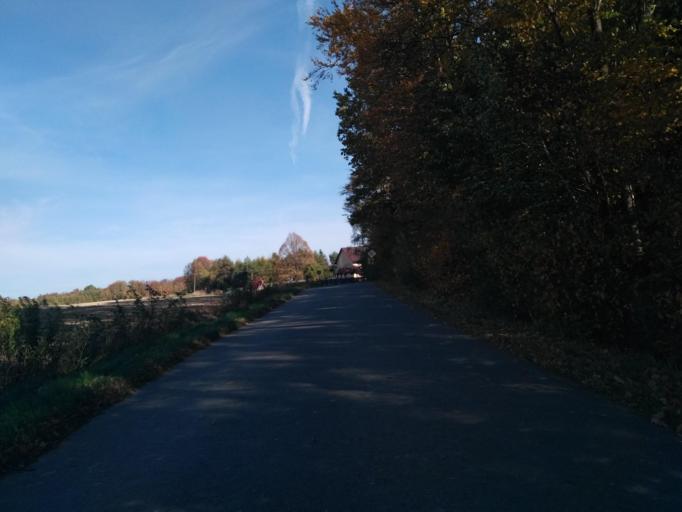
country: PL
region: Subcarpathian Voivodeship
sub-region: Powiat ropczycko-sedziszowski
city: Zagorzyce
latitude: 49.9963
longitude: 21.7059
